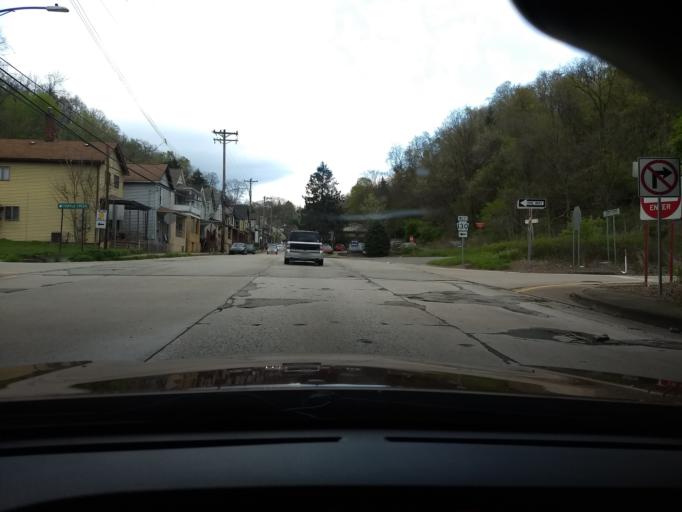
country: US
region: Pennsylvania
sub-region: Allegheny County
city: Wilmerding
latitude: 40.3964
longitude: -79.8046
